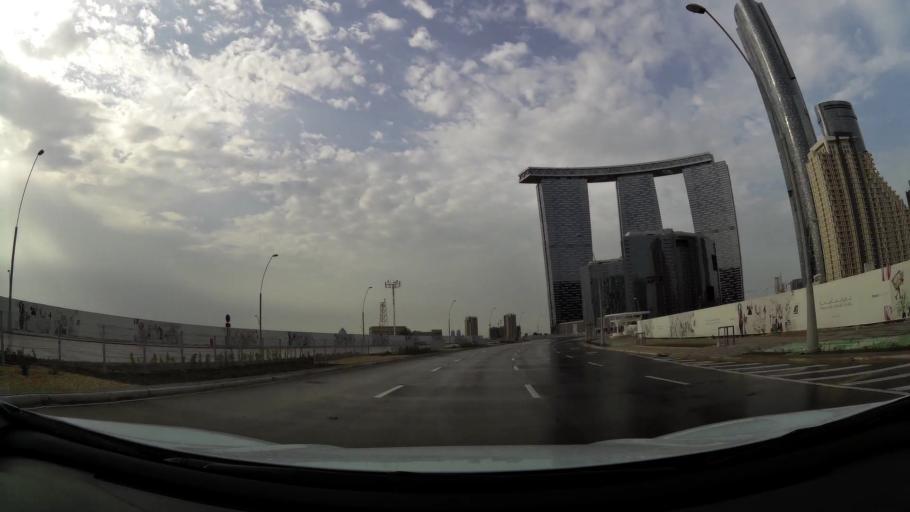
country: AE
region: Abu Dhabi
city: Abu Dhabi
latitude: 24.4970
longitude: 54.4124
